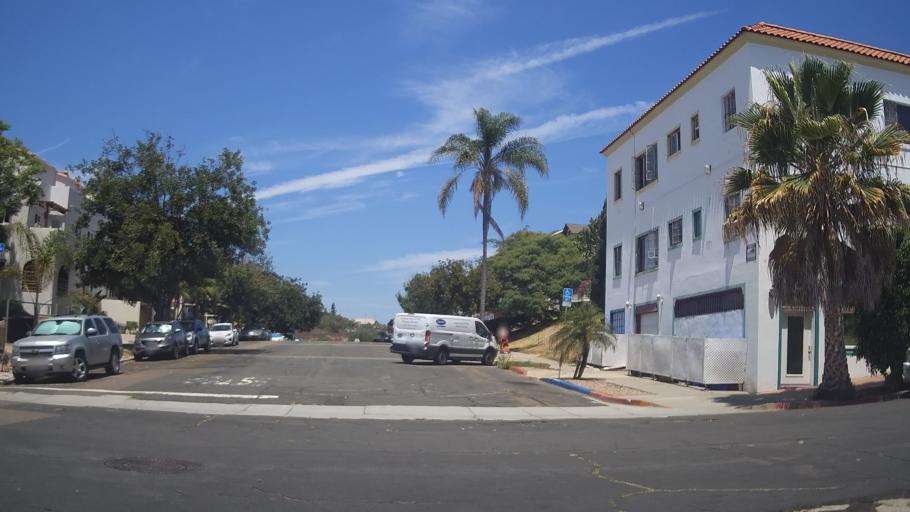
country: US
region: California
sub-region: San Diego County
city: San Diego
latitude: 32.7168
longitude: -117.1449
